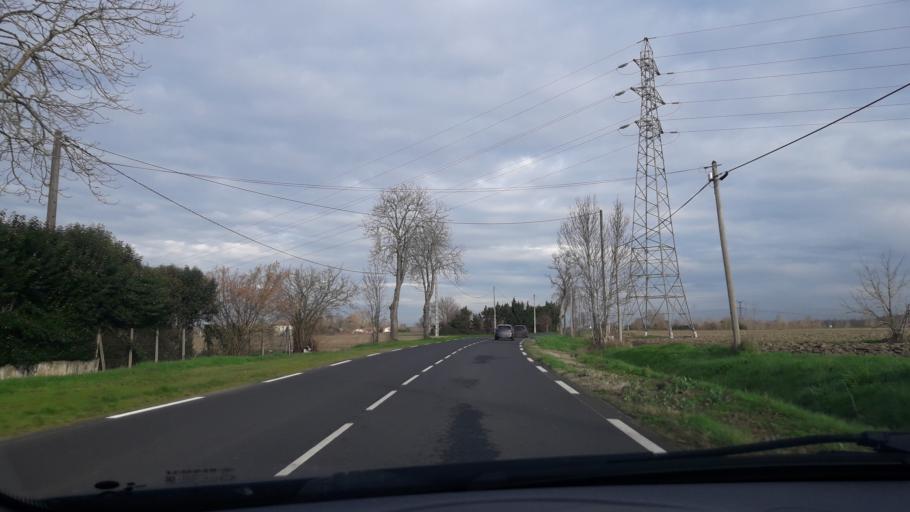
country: FR
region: Midi-Pyrenees
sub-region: Departement de la Haute-Garonne
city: Ondes
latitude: 43.7901
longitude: 1.2980
